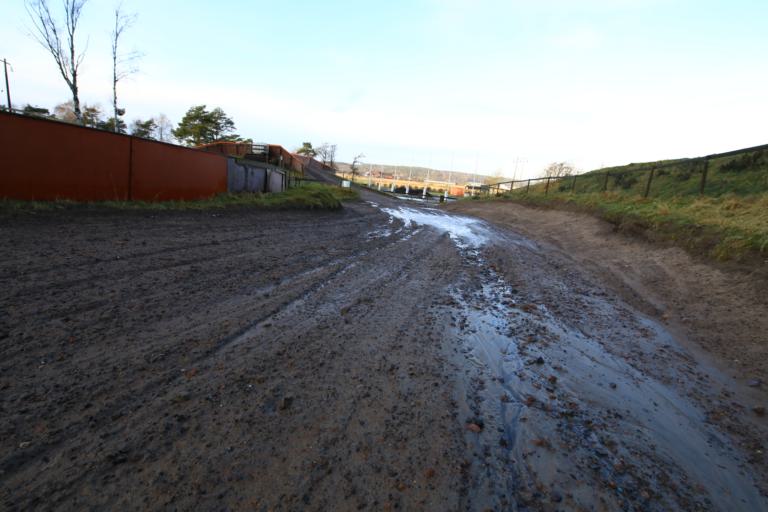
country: SE
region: Halland
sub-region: Varbergs Kommun
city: Varberg
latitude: 57.1514
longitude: 12.2838
